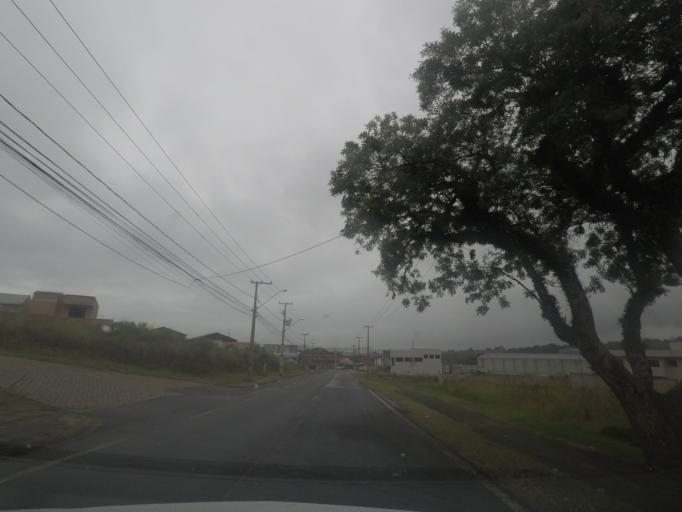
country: BR
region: Parana
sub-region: Quatro Barras
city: Quatro Barras
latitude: -25.3701
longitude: -49.0798
